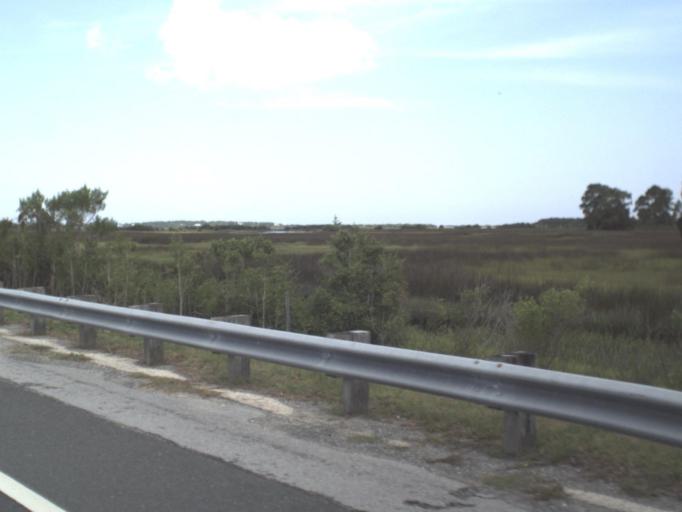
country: US
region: Florida
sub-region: Levy County
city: Chiefland
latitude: 29.1720
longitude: -83.0257
